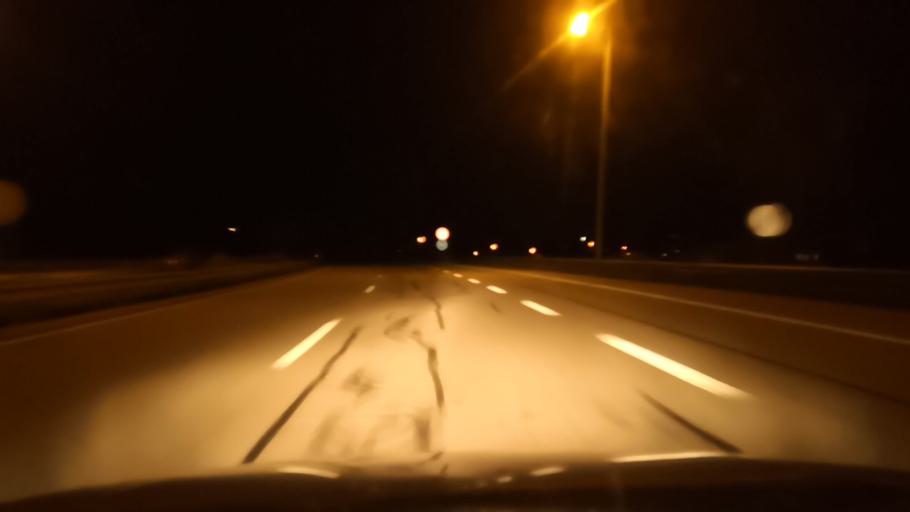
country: PT
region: Evora
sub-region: Estremoz
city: Estremoz
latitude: 38.8422
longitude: -7.6120
